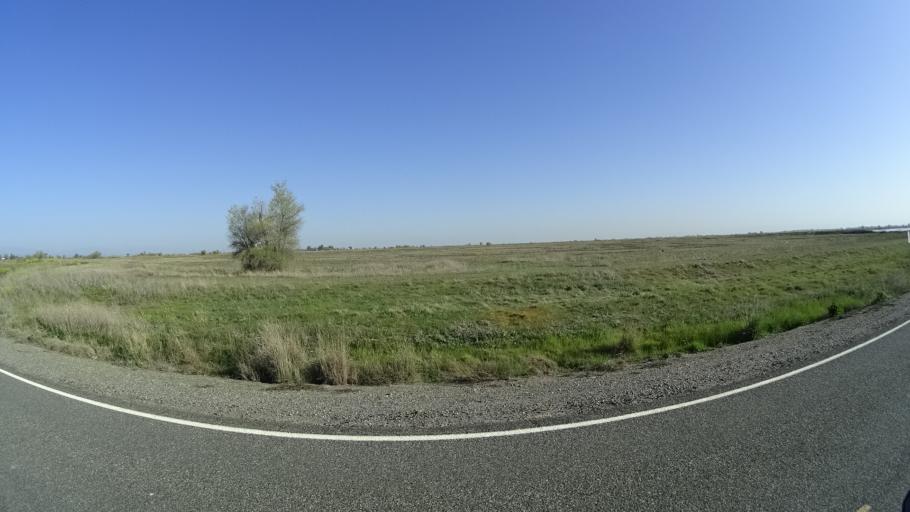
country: US
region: California
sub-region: Glenn County
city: Willows
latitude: 39.4072
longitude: -122.1766
